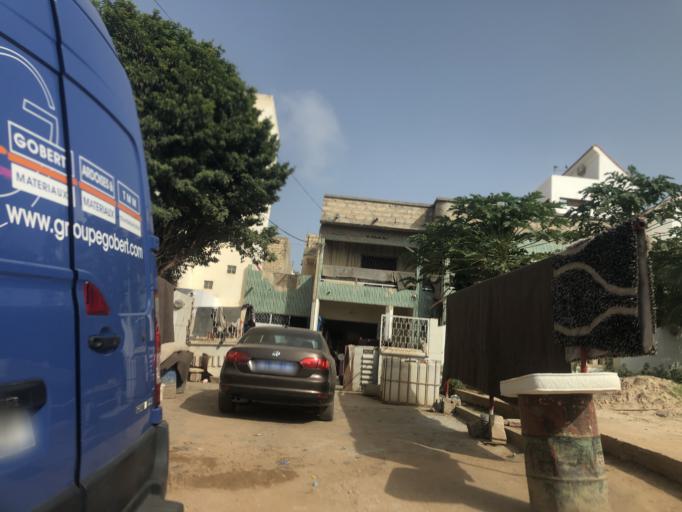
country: SN
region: Dakar
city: Mermoz Boabab
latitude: 14.7321
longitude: -17.4983
